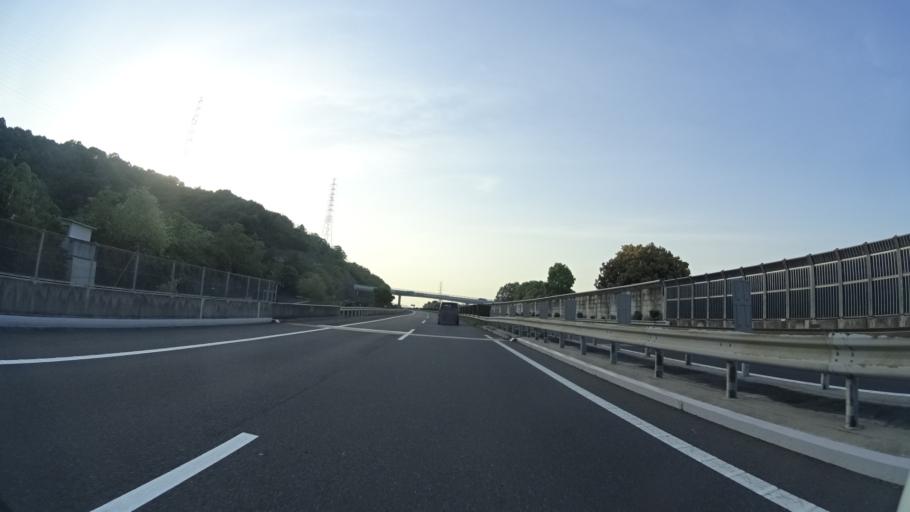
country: JP
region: Kagawa
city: Sakaidecho
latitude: 34.3187
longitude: 133.8362
